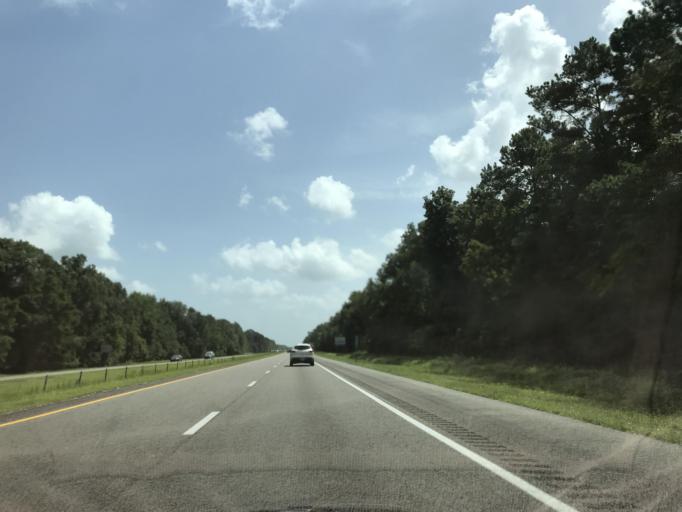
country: US
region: North Carolina
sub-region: Pender County
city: Rocky Point
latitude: 34.4565
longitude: -77.8789
